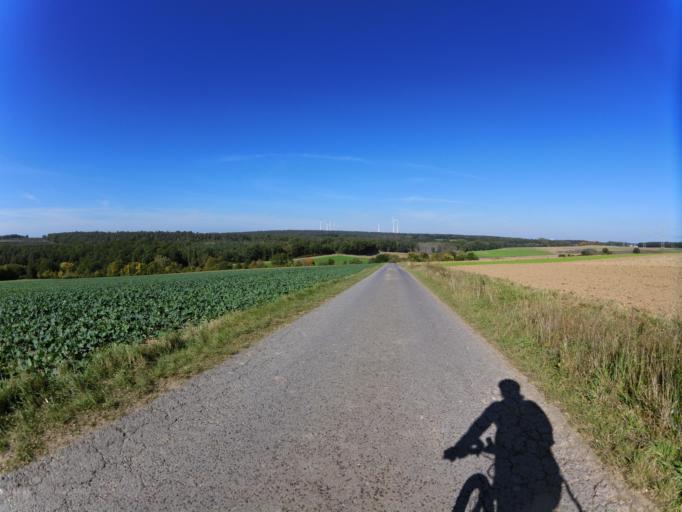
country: DE
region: Bavaria
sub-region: Regierungsbezirk Unterfranken
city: Ochsenfurt
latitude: 49.6875
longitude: 10.0569
